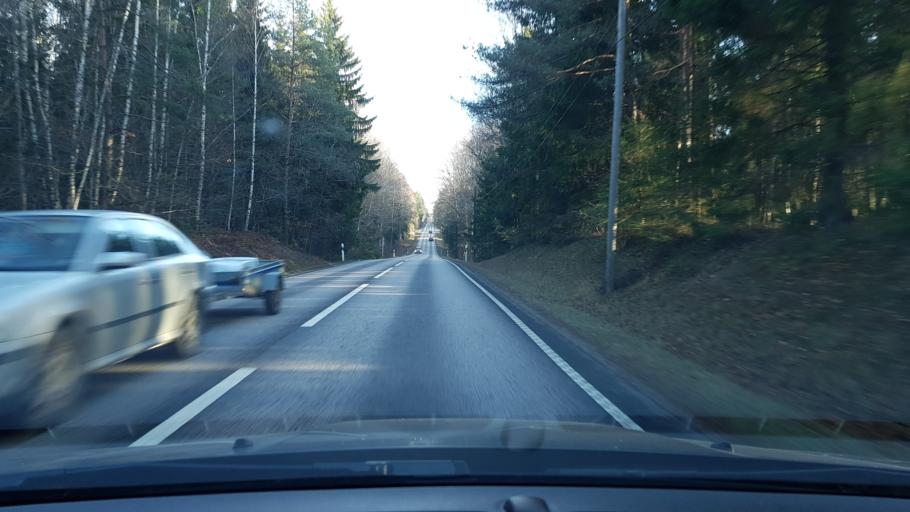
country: SE
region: Stockholm
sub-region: Norrtalje Kommun
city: Rimbo
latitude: 59.7407
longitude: 18.3136
